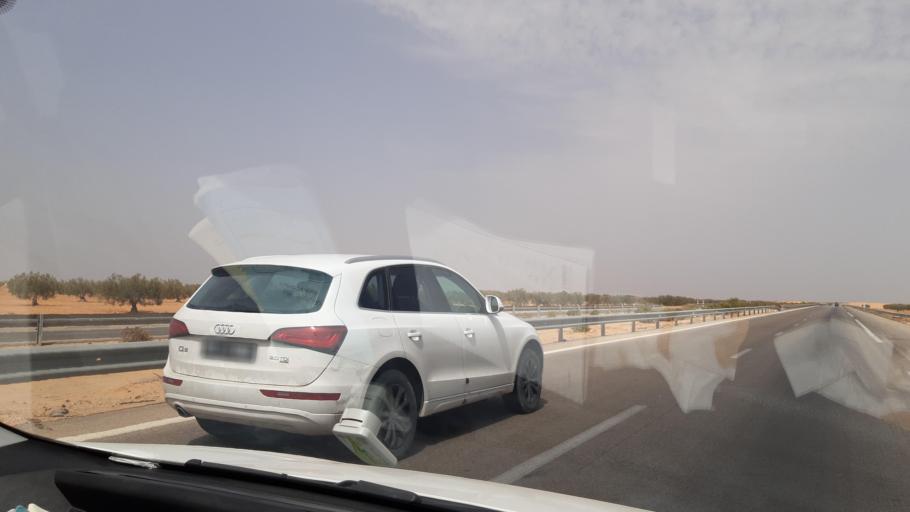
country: TN
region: Safaqis
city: Bi'r `Ali Bin Khalifah
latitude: 34.5700
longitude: 10.3794
